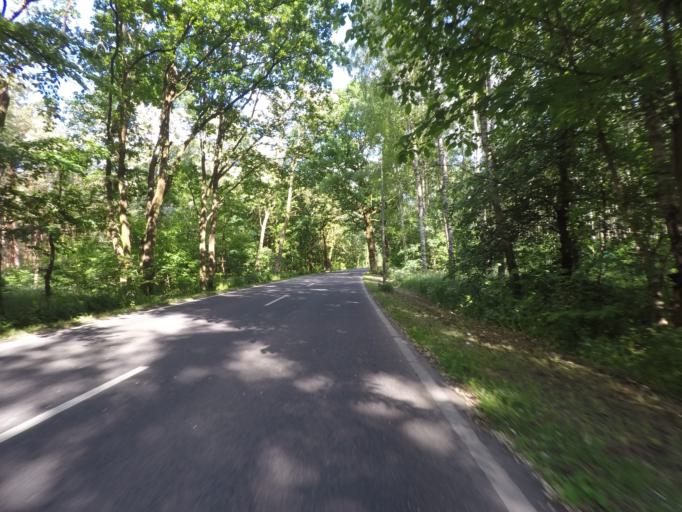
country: DE
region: Brandenburg
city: Britz
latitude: 52.8591
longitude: 13.7907
